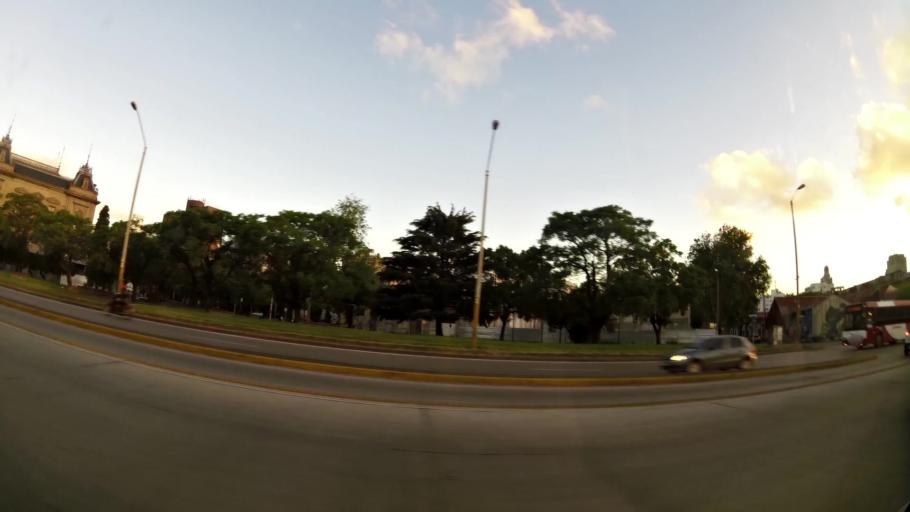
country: UY
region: Montevideo
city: Montevideo
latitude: -34.8993
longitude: -56.1952
